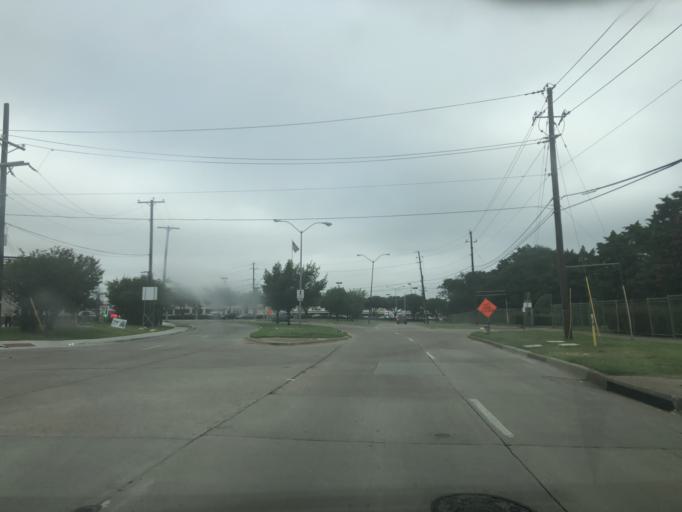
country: US
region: Texas
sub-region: Dallas County
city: University Park
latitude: 32.8659
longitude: -96.8635
